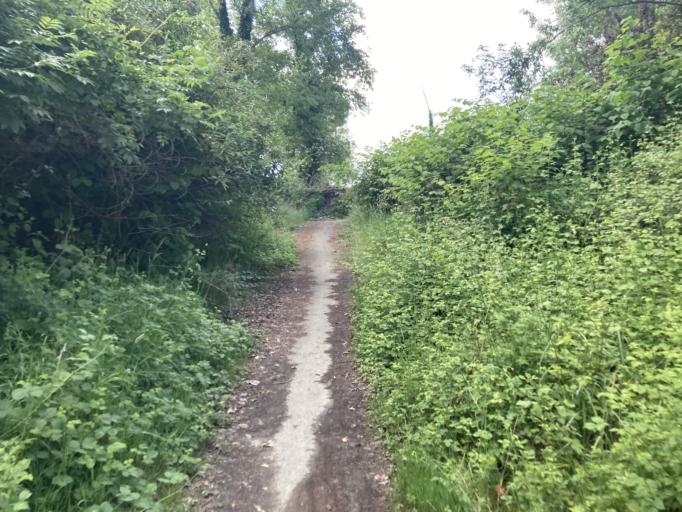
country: FR
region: Aquitaine
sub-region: Departement des Pyrenees-Atlantiques
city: Arbus
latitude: 43.3428
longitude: -0.5041
